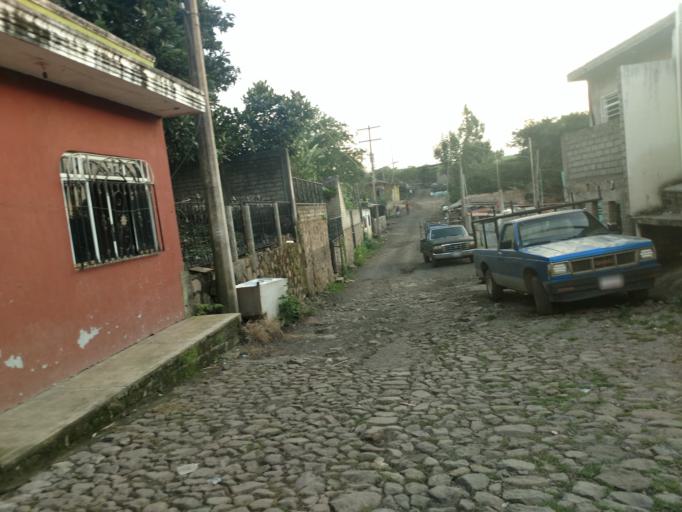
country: MX
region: Nayarit
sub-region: Tepic
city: La Corregidora
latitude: 21.4592
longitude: -104.8005
